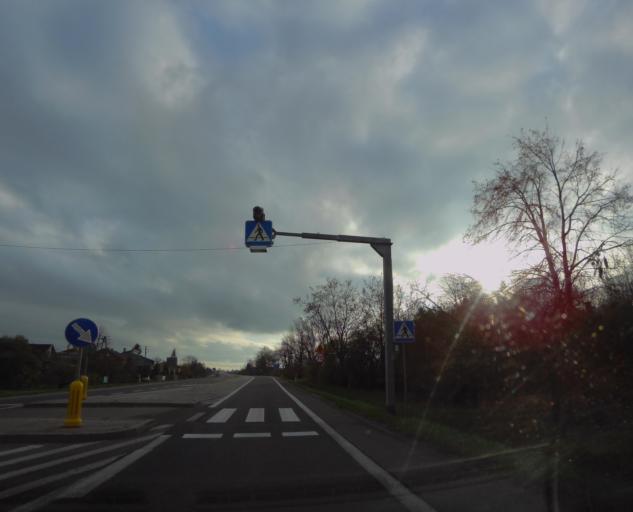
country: PL
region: Subcarpathian Voivodeship
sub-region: Powiat przemyski
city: Orly
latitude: 49.9006
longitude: 22.8167
